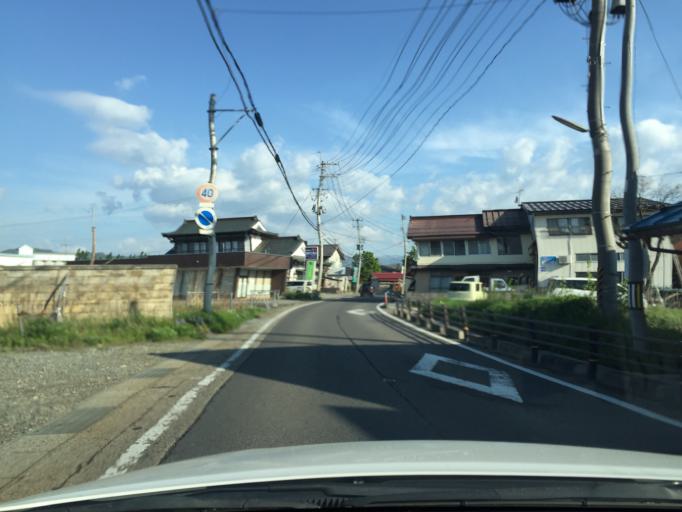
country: JP
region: Fukushima
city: Kitakata
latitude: 37.6756
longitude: 139.8716
